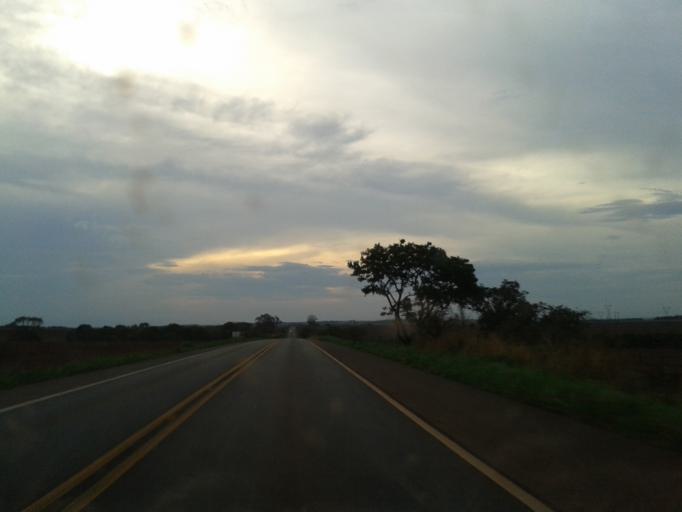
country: BR
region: Goias
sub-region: Santa Helena De Goias
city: Santa Helena de Goias
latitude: -17.8892
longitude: -50.6713
